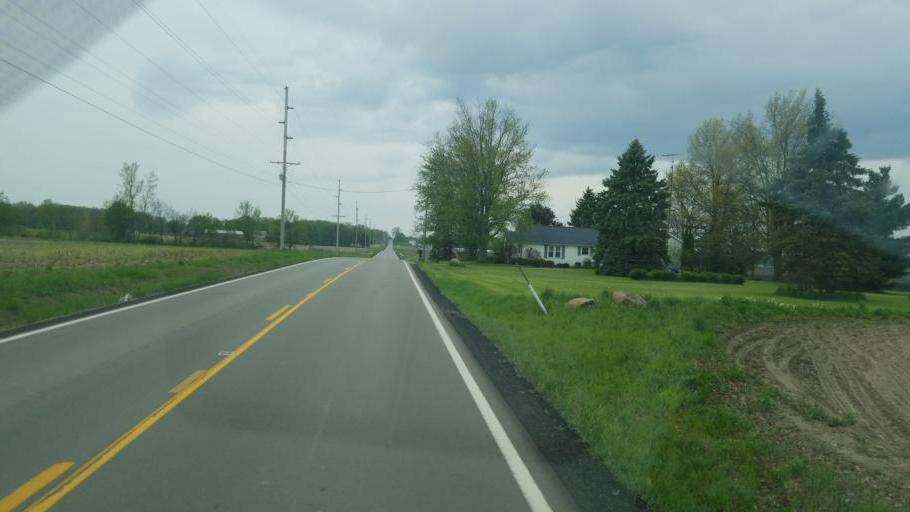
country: US
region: Ohio
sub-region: Huron County
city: Plymouth
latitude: 41.0158
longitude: -82.6904
